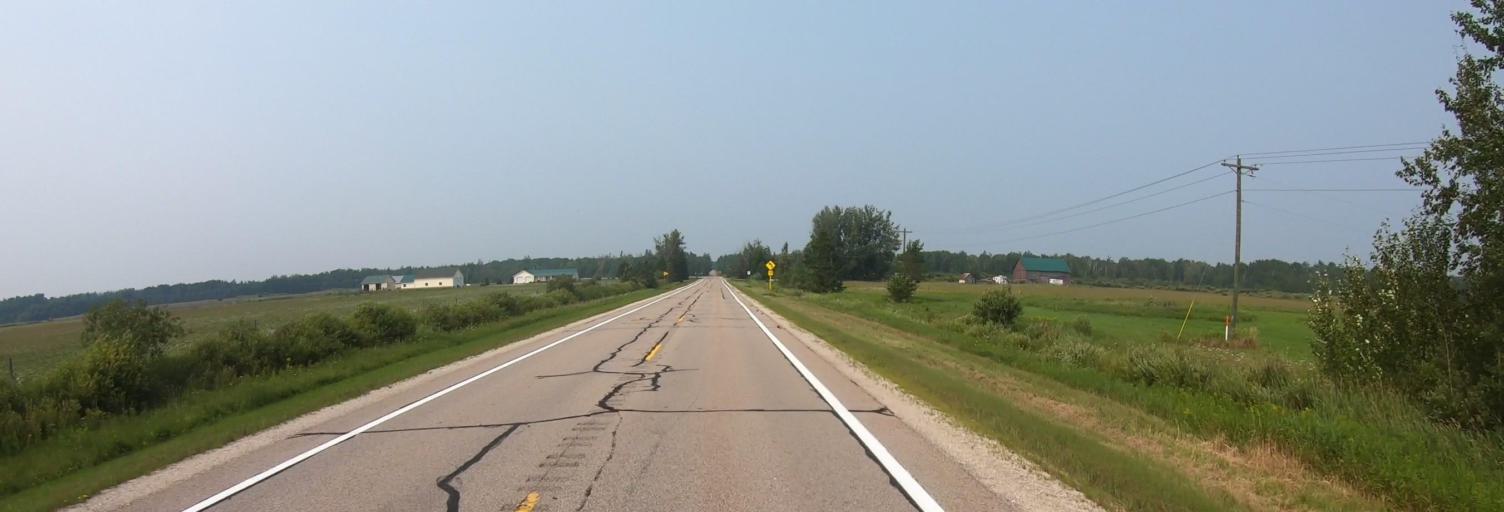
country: US
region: Michigan
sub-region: Chippewa County
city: Sault Ste. Marie
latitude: 46.1228
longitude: -84.2595
